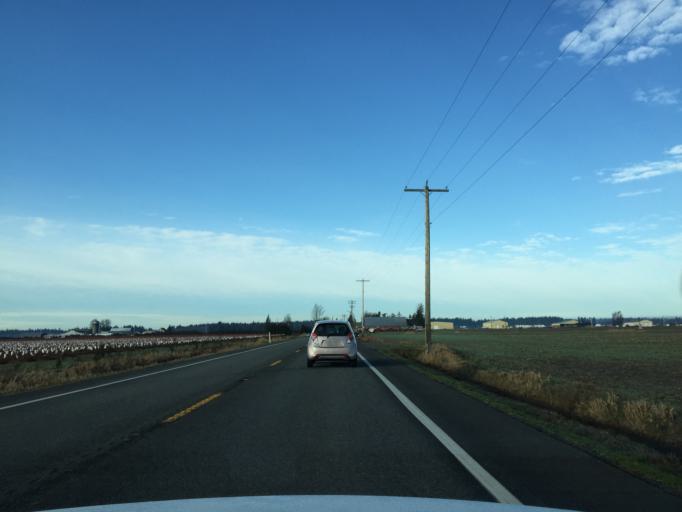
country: US
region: Washington
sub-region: Whatcom County
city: Lynden
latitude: 48.9644
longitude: -122.4765
